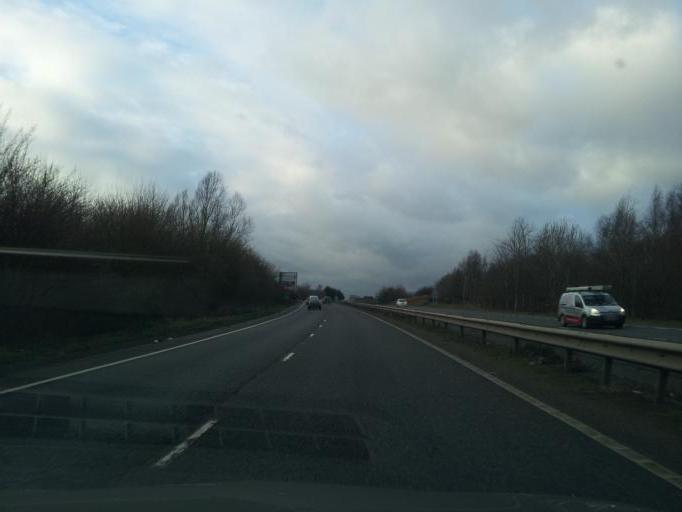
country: GB
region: England
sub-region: Norfolk
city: Bowthorpe
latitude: 52.6212
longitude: 1.2043
